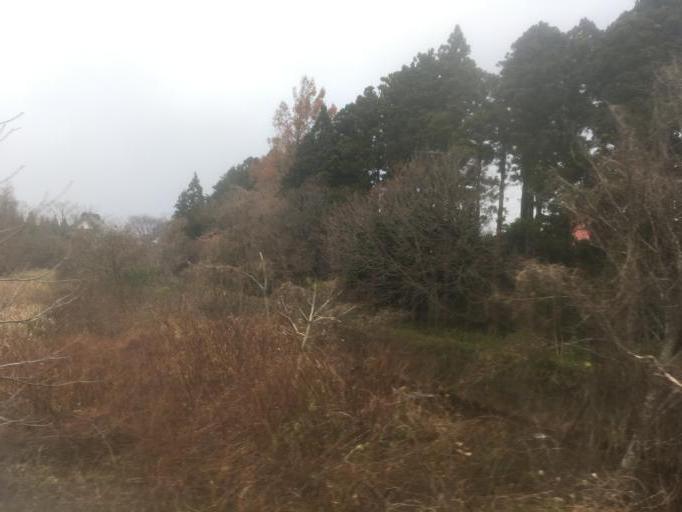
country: JP
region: Aomori
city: Goshogawara
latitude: 41.1806
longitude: 140.4781
